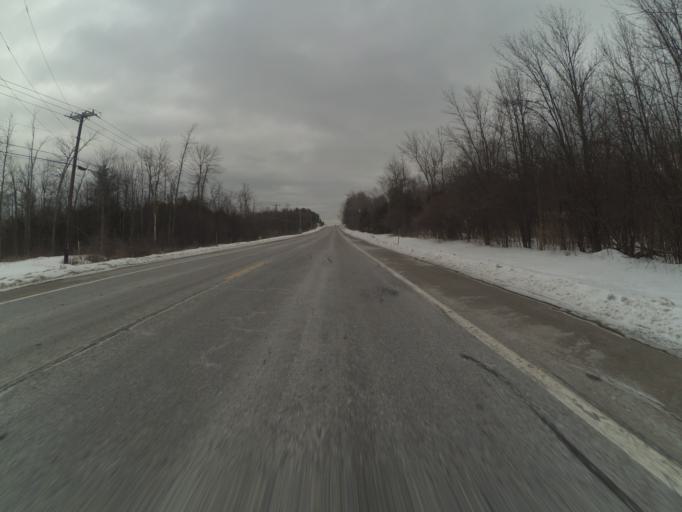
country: US
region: New York
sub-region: St. Lawrence County
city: Potsdam
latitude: 44.6994
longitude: -74.9406
